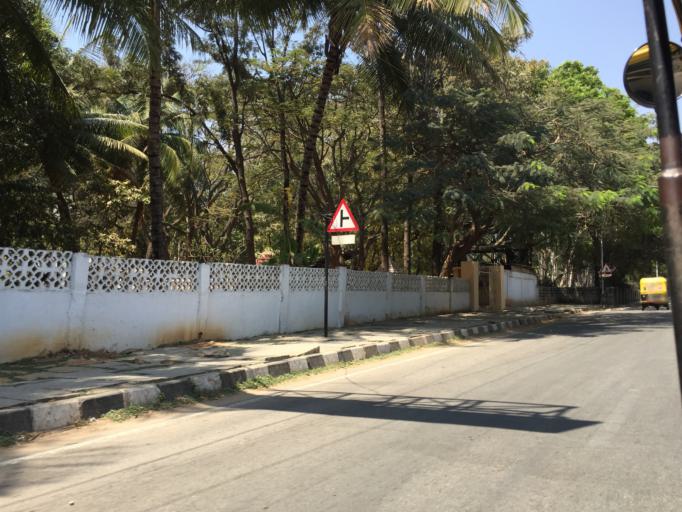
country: IN
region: Karnataka
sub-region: Bangalore Urban
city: Bangalore
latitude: 12.9922
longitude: 77.6191
